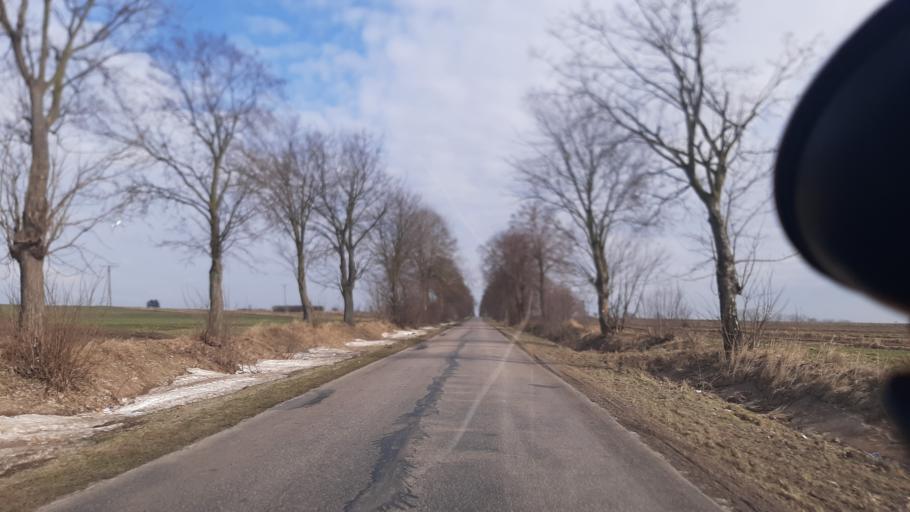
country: PL
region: Lublin Voivodeship
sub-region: Powiat lubartowski
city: Wola Sernicka
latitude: 51.4554
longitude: 22.6835
